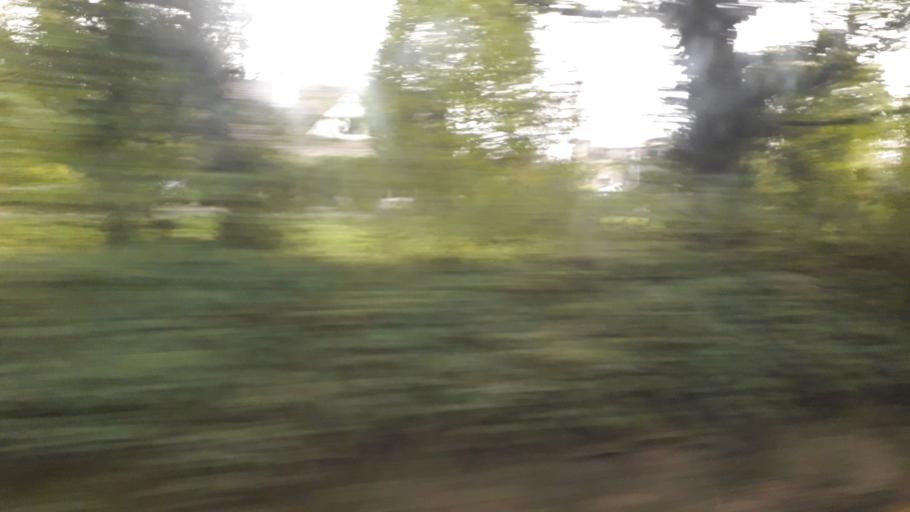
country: IE
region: Munster
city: Ballina
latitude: 52.7937
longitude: -8.4347
